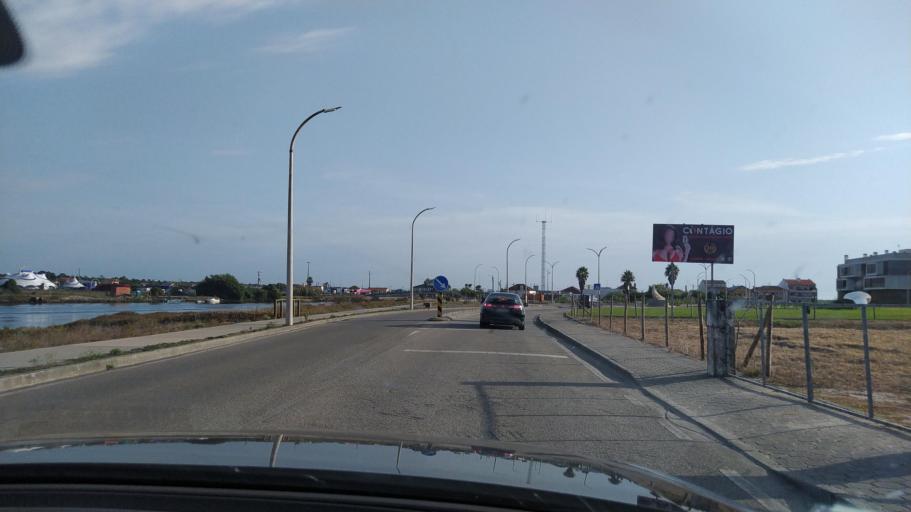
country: PT
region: Aveiro
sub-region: Ilhavo
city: Gafanha da Encarnacao
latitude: 40.5634
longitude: -8.7573
